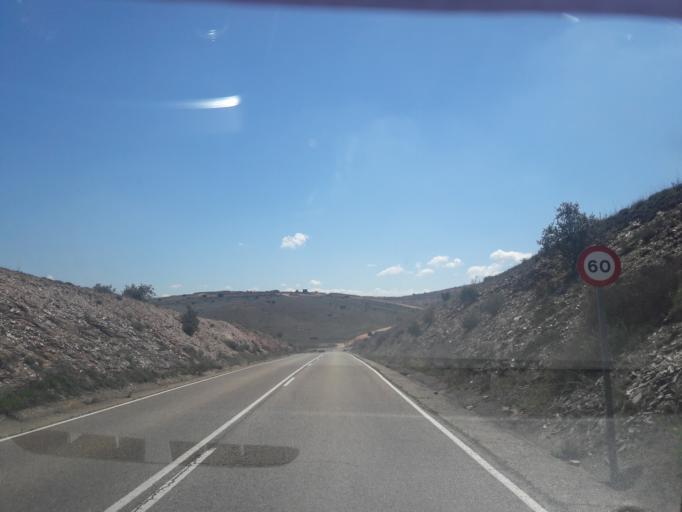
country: ES
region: Castille and Leon
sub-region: Provincia de Salamanca
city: Doninos de Salamanca
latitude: 40.9388
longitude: -5.7224
